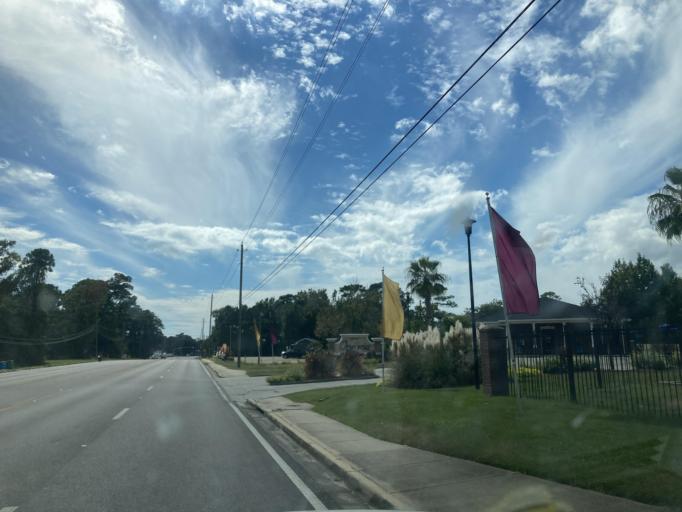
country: US
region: Mississippi
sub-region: Jackson County
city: Saint Martin
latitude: 30.4399
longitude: -88.8771
